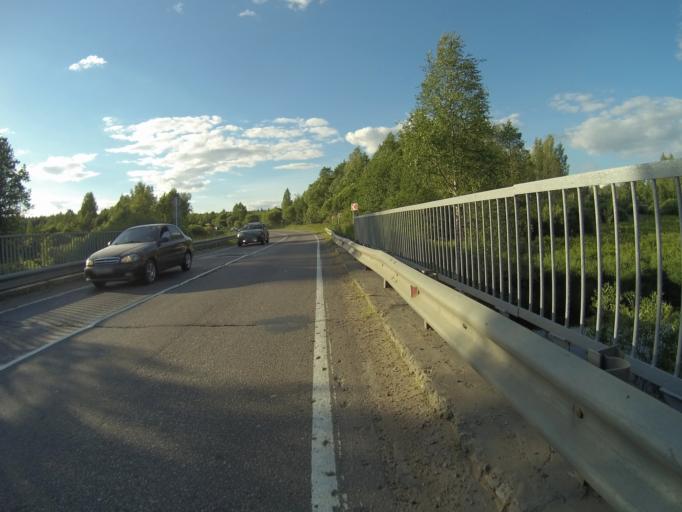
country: RU
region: Vladimir
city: Anopino
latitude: 55.8518
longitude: 40.6449
